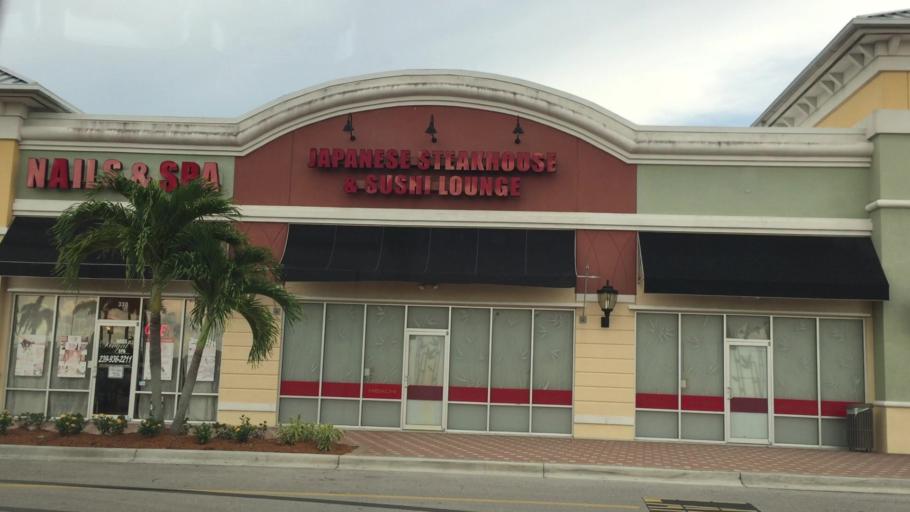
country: US
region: Florida
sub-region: Lee County
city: Fort Myers
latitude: 26.6033
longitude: -81.8090
